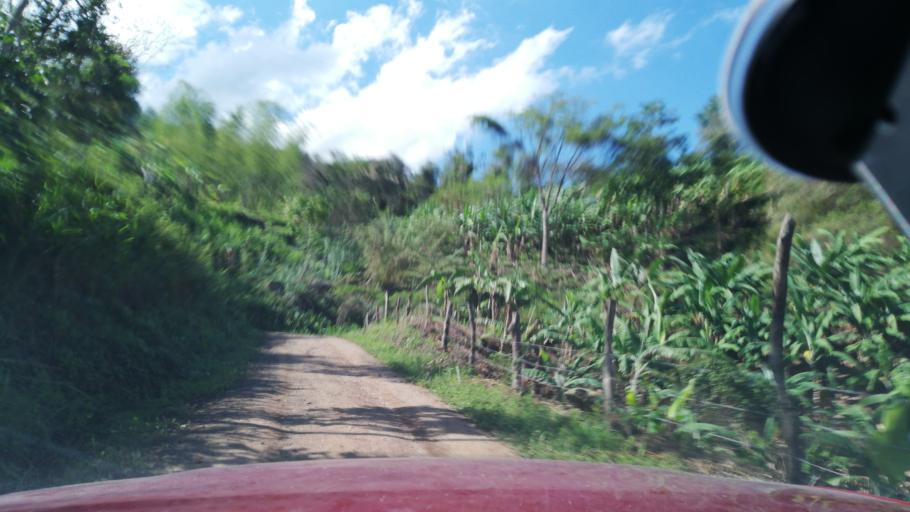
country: CO
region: Cundinamarca
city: Quipile
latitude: 4.7471
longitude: -74.6127
